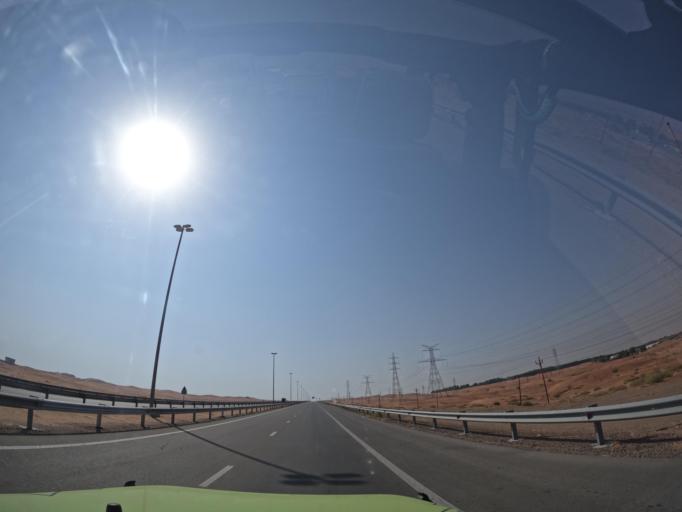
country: OM
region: Al Buraimi
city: Al Buraymi
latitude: 24.3549
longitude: 55.7346
